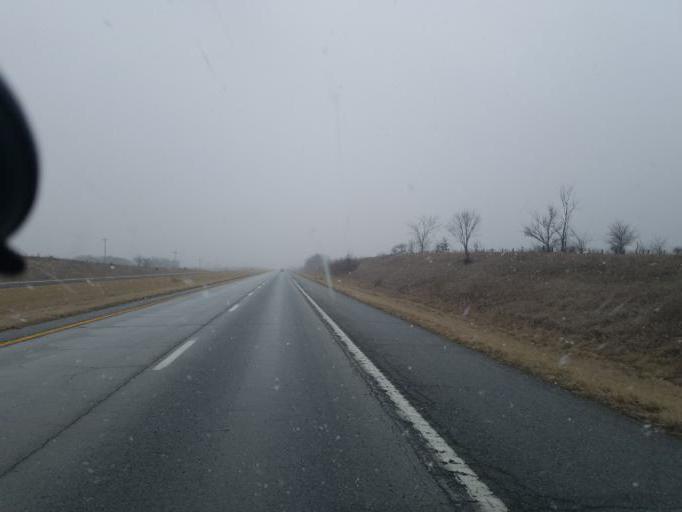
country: US
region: Missouri
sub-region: Macon County
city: La Plata
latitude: 39.9683
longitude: -92.4765
